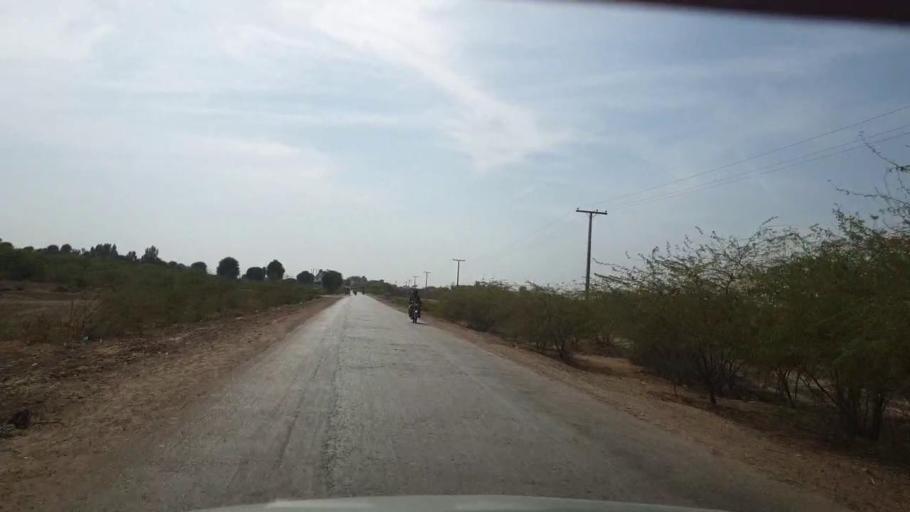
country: PK
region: Sindh
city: Kunri
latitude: 25.1715
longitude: 69.5315
